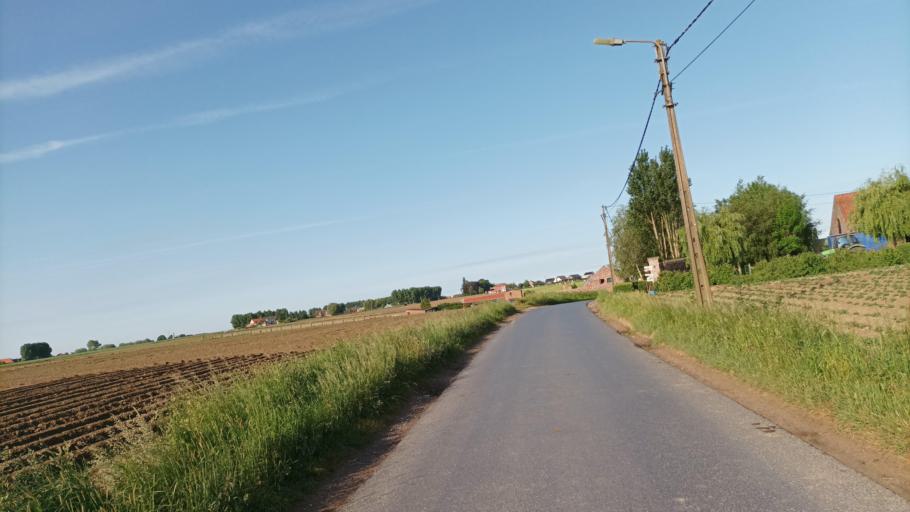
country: BE
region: Flanders
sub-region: Provincie West-Vlaanderen
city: Moorslede
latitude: 50.8453
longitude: 3.0700
